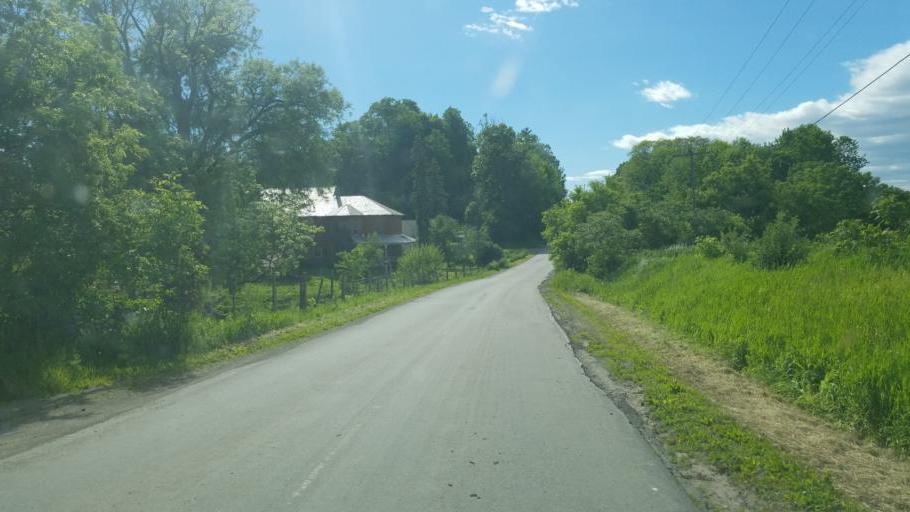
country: US
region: New York
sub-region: Montgomery County
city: Saint Johnsville
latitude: 42.9889
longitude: -74.6732
